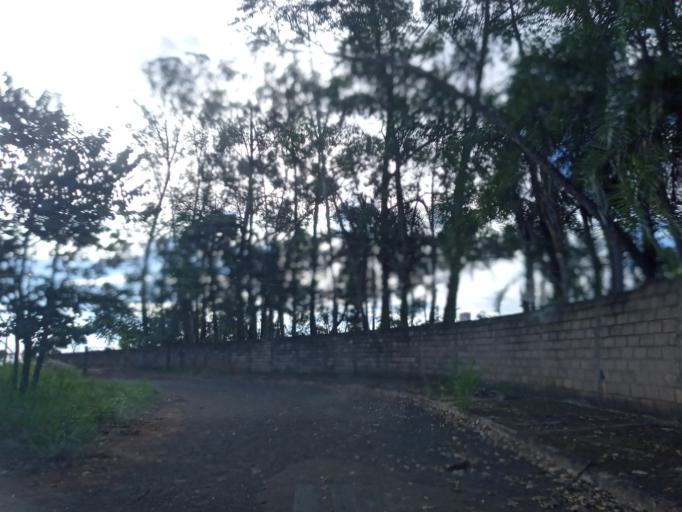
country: BR
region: Minas Gerais
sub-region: Ituiutaba
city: Ituiutaba
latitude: -18.9641
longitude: -49.4964
